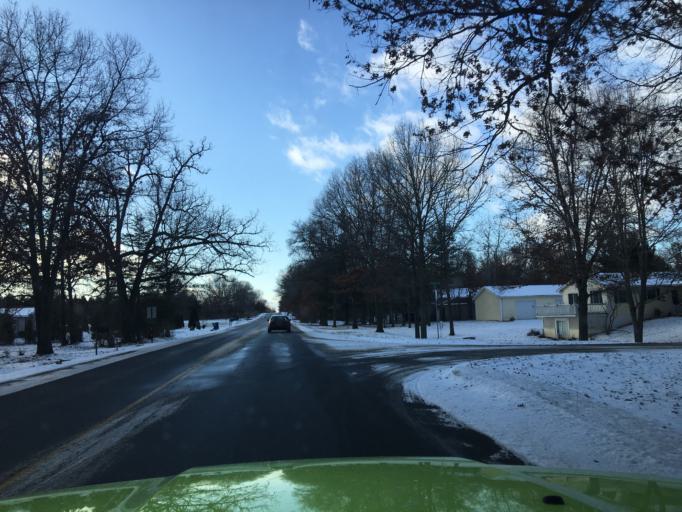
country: US
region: Michigan
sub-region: Montcalm County
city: Greenville
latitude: 43.2064
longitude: -85.2749
